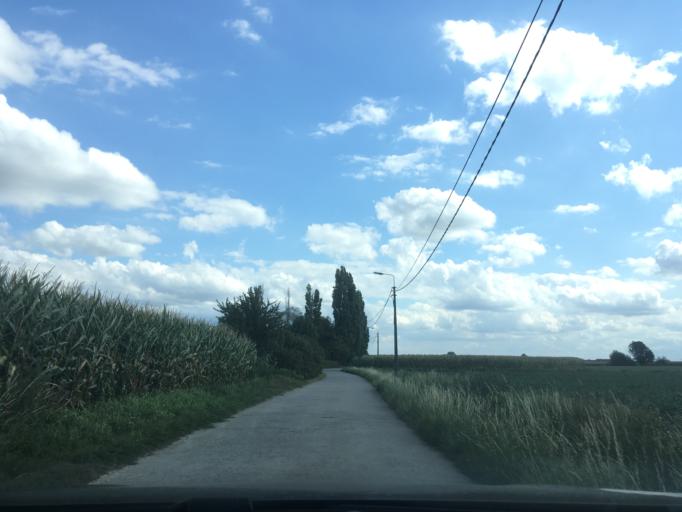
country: BE
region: Flanders
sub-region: Provincie West-Vlaanderen
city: Staden
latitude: 50.9806
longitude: 3.0381
